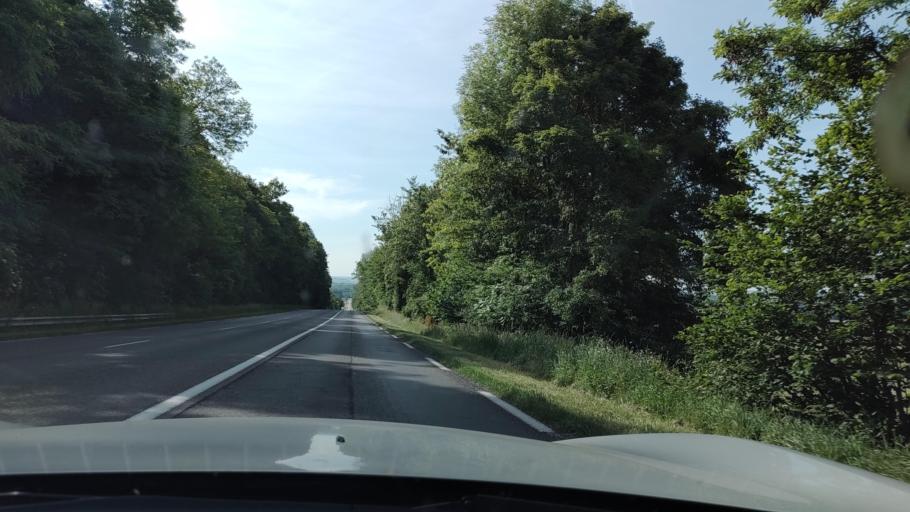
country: FR
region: Ile-de-France
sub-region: Departement de Seine-et-Marne
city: Sourdun
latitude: 48.5246
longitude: 3.4100
